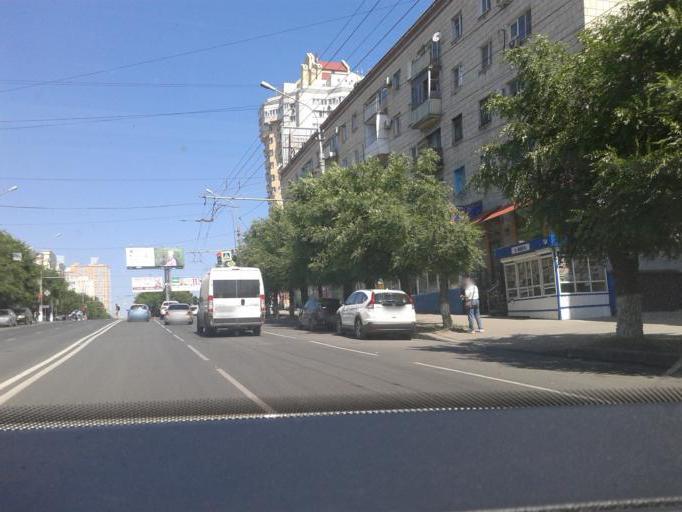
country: RU
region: Volgograd
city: Volgograd
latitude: 48.7153
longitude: 44.5116
